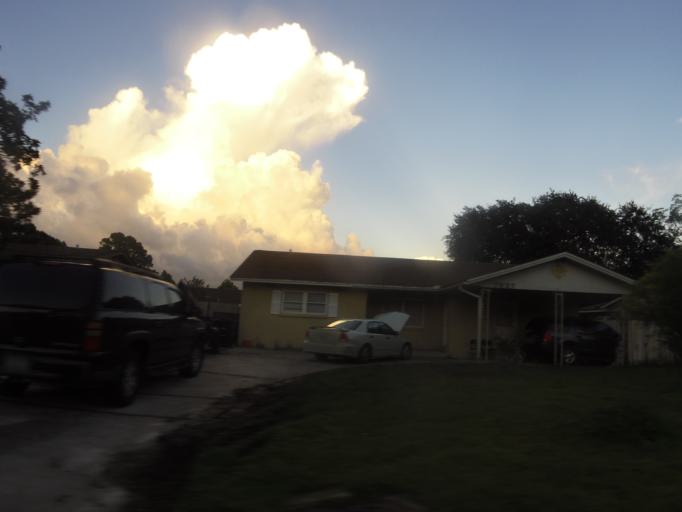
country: US
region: Florida
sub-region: Duval County
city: Jacksonville
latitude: 30.2380
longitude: -81.6049
